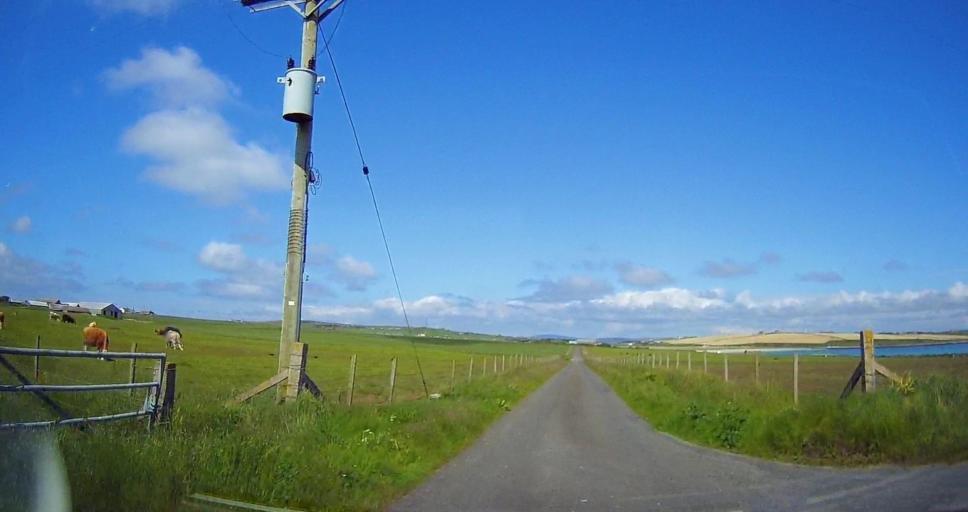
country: GB
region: Scotland
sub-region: Orkney Islands
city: Kirkwall
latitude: 58.8318
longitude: -2.8987
